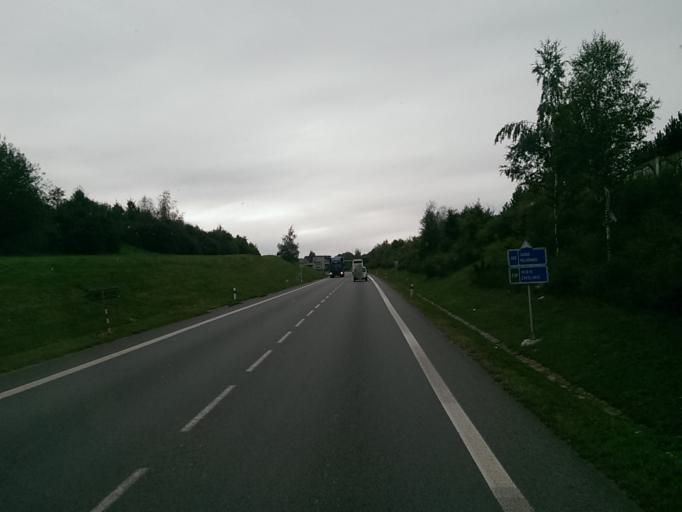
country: CZ
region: Vysocina
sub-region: Okres Jihlava
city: Jihlava
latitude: 49.4045
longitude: 15.5690
